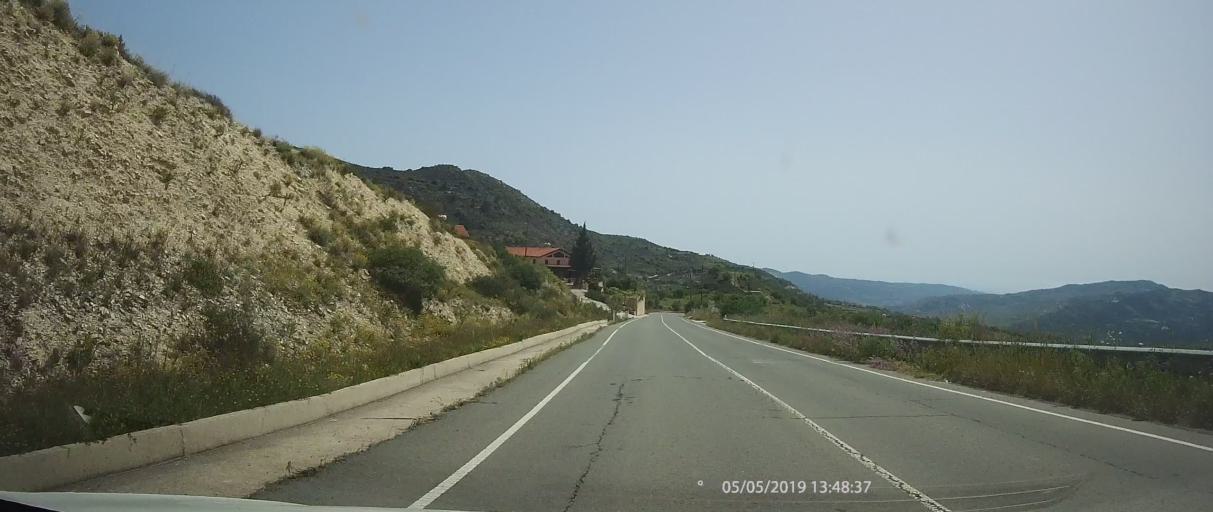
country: CY
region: Limassol
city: Pachna
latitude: 34.8562
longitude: 32.7518
